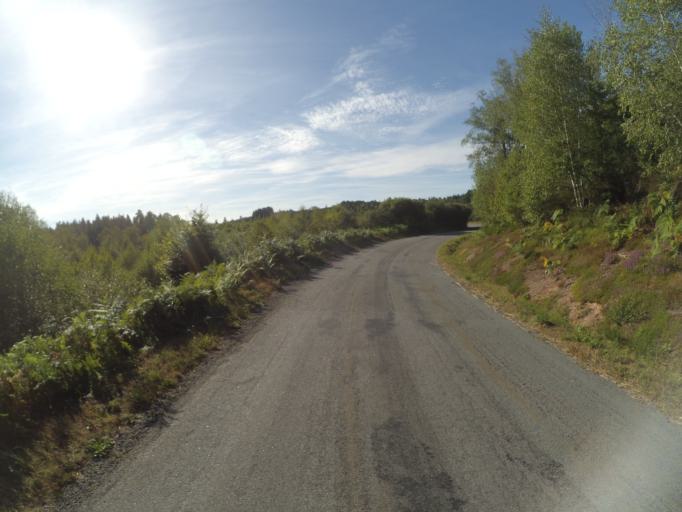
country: FR
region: Limousin
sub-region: Departement de la Correze
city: Bugeat
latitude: 45.7025
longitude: 2.0192
